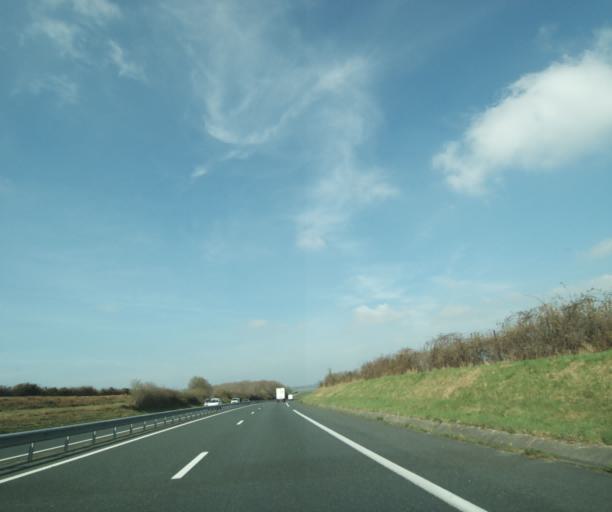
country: FR
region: Centre
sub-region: Departement de l'Indre
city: Chantome
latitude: 46.4895
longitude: 1.4987
